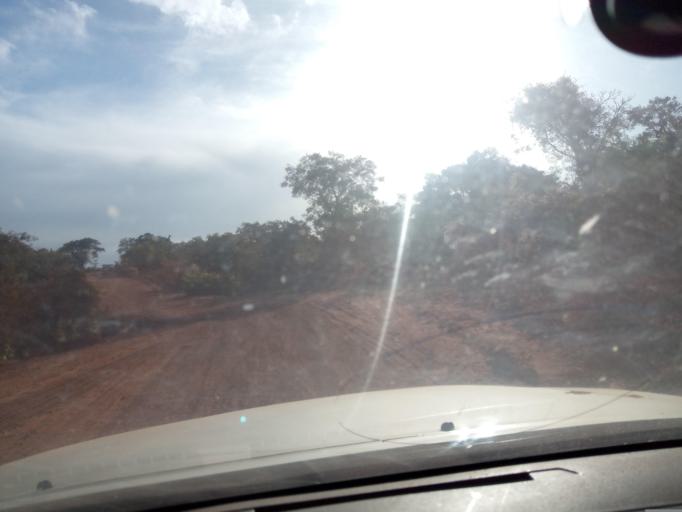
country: ML
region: Sikasso
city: Sikasso
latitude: 11.4143
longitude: -5.5688
